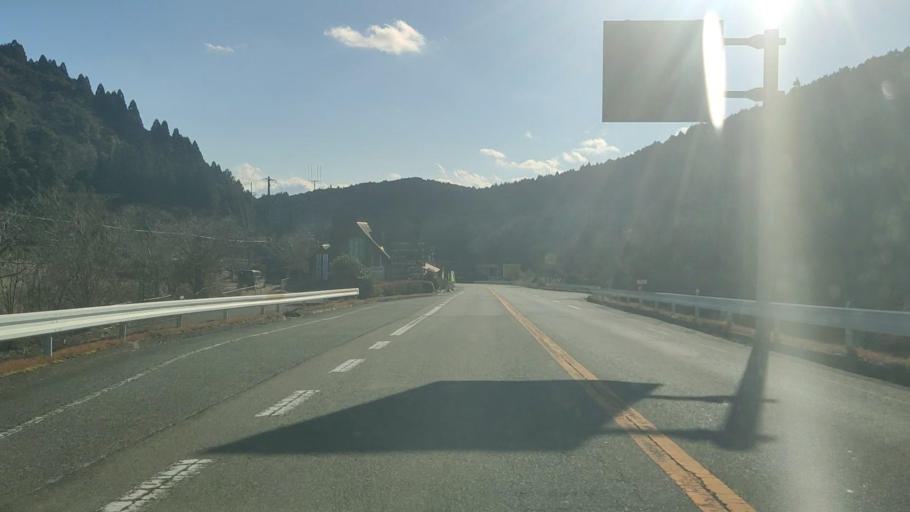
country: JP
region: Fukuoka
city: Maebaru-chuo
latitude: 33.4610
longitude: 130.2745
